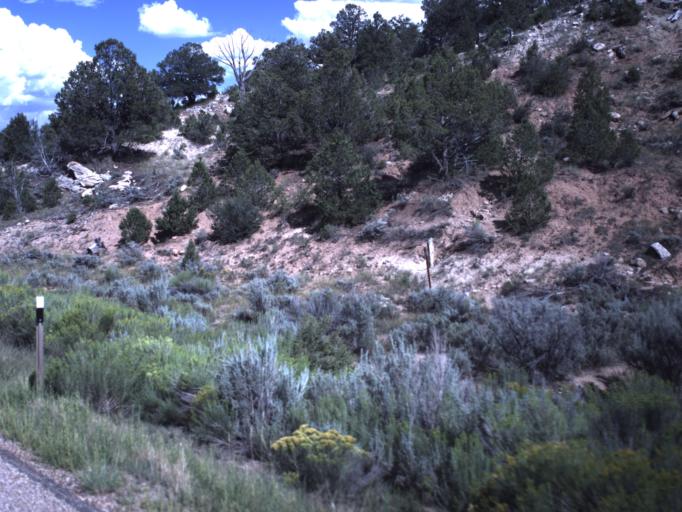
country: US
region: Utah
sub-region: Duchesne County
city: Duchesne
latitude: 40.3205
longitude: -110.6933
